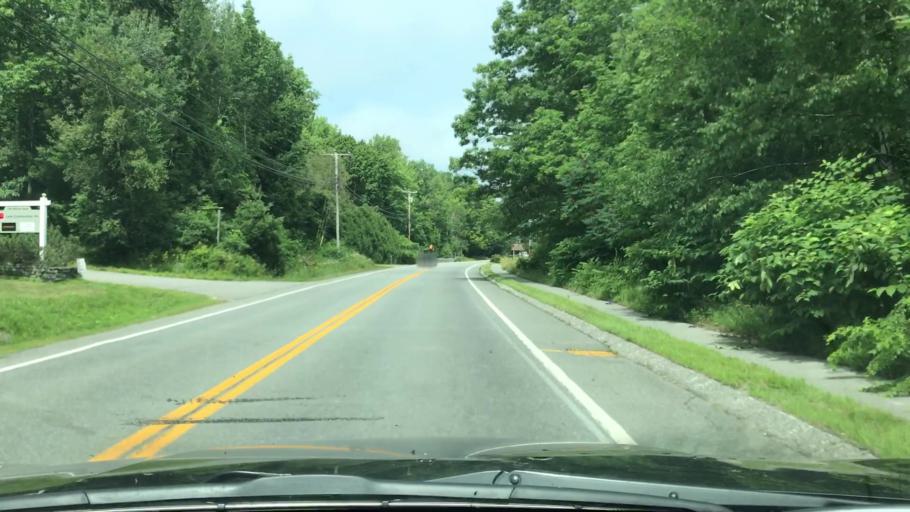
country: US
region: Maine
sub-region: Knox County
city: Camden
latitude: 44.2258
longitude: -69.0504
